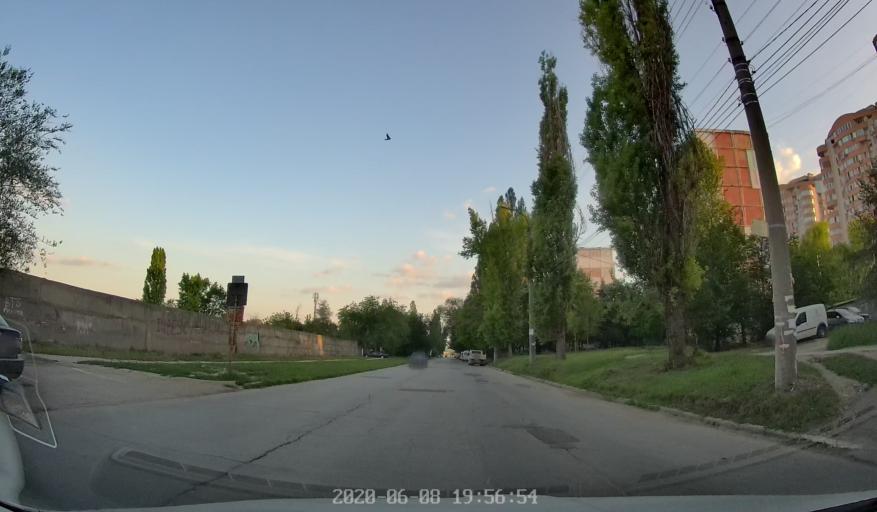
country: MD
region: Chisinau
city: Chisinau
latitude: 47.0192
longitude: 28.8828
